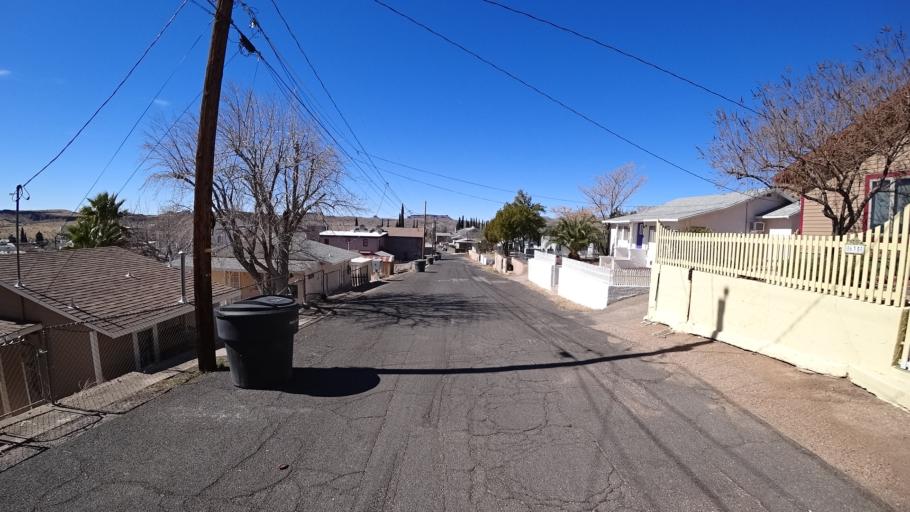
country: US
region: Arizona
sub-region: Mohave County
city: Kingman
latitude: 35.1904
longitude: -114.0479
